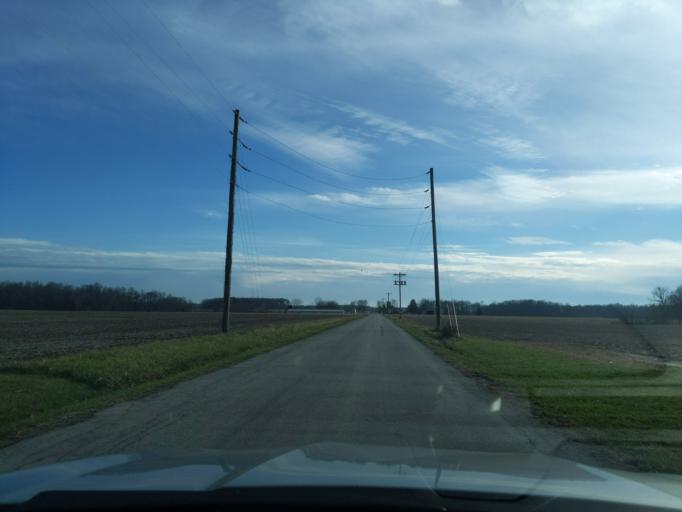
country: US
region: Indiana
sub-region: Decatur County
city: Westport
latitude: 39.2174
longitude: -85.4652
